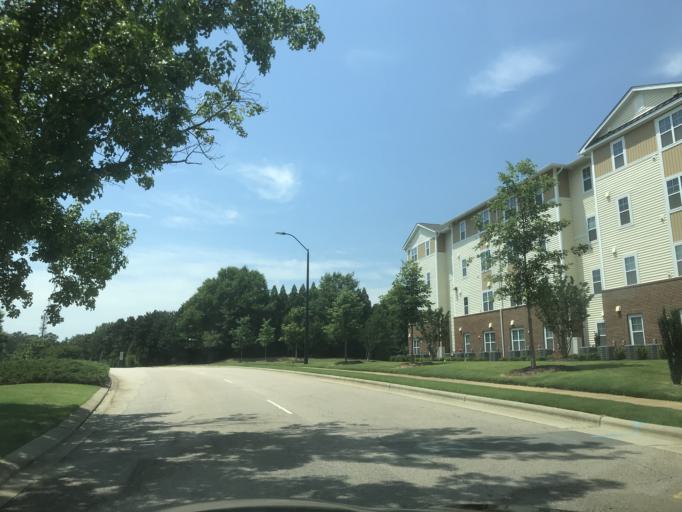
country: US
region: North Carolina
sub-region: Wake County
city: Wake Forest
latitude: 35.9444
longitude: -78.5611
